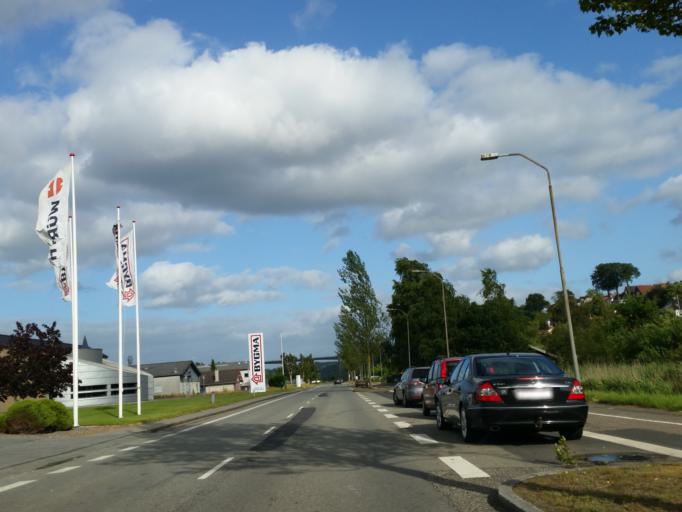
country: DK
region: South Denmark
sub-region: Vejle Kommune
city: Vejle
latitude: 55.7005
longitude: 9.5498
